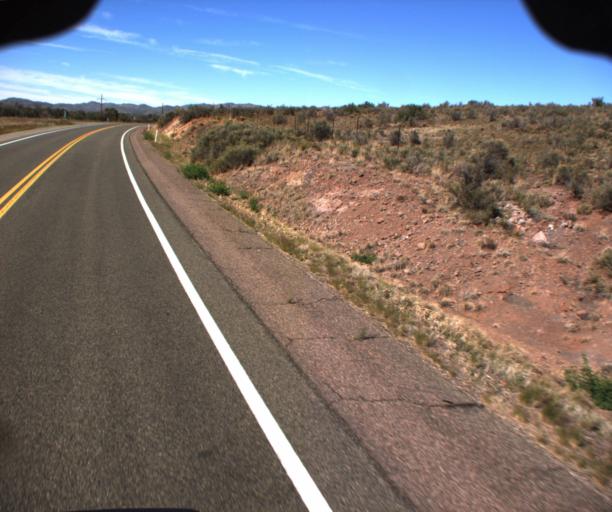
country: US
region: Arizona
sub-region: Yavapai County
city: Congress
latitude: 34.3113
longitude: -112.7095
